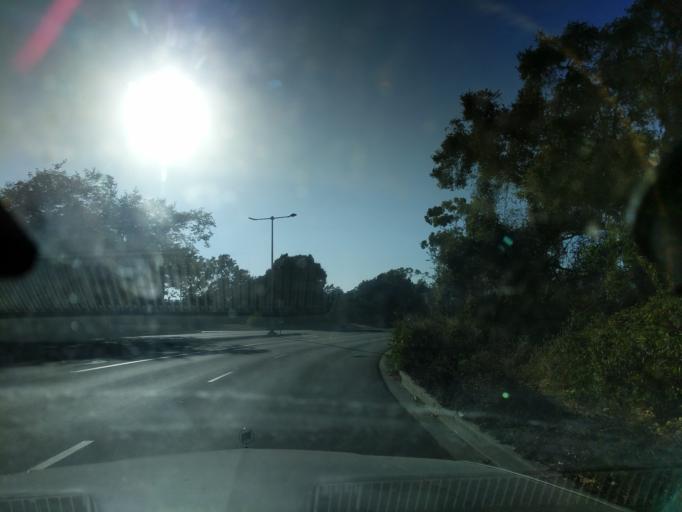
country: US
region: California
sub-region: Santa Barbara County
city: Isla Vista
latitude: 34.4161
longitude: -119.8421
